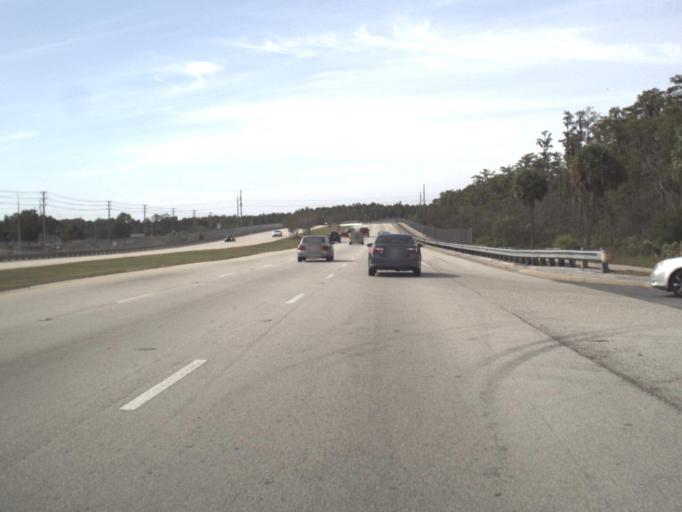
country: US
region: Florida
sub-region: Orange County
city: Oak Ridge
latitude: 28.4606
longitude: -81.4229
